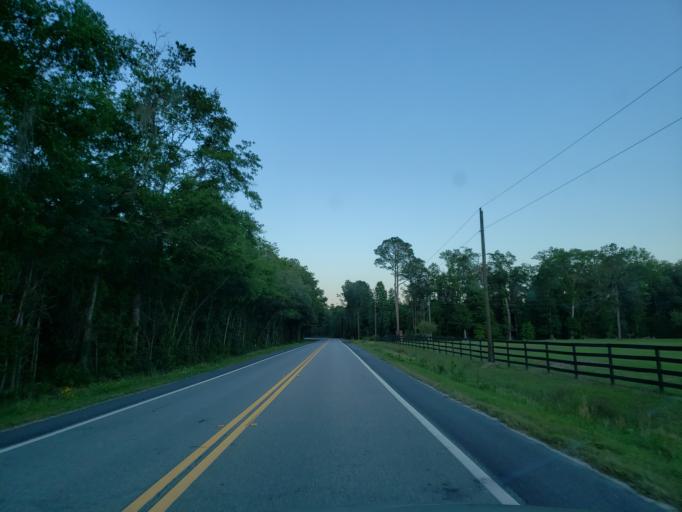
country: US
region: Georgia
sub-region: Echols County
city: Statenville
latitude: 30.5627
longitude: -83.1479
